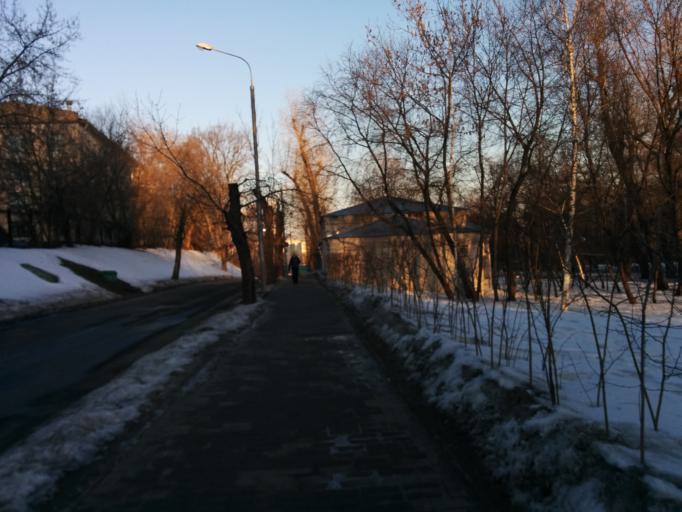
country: RU
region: Moscow
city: Novyye Cheremushki
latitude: 55.7218
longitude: 37.5983
